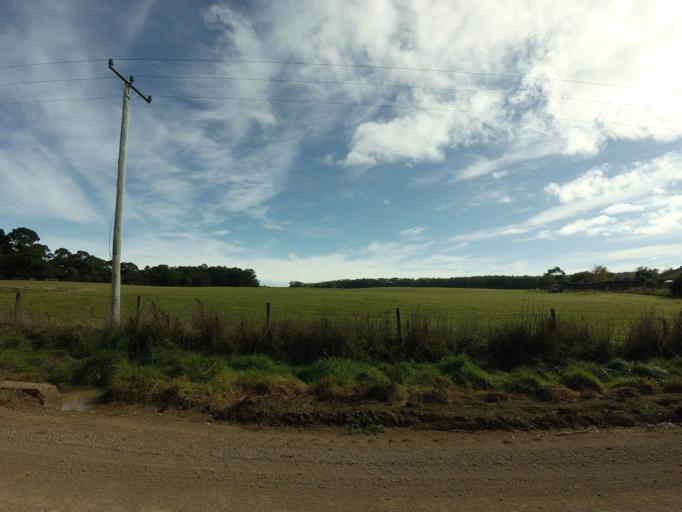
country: AU
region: Tasmania
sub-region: Clarence
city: Sandford
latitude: -43.1609
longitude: 147.7683
